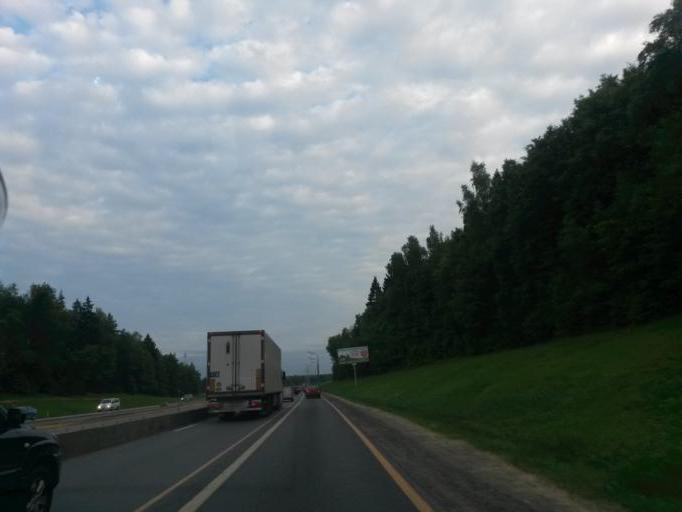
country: RU
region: Moskovskaya
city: Lyubuchany
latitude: 55.2401
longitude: 37.5268
